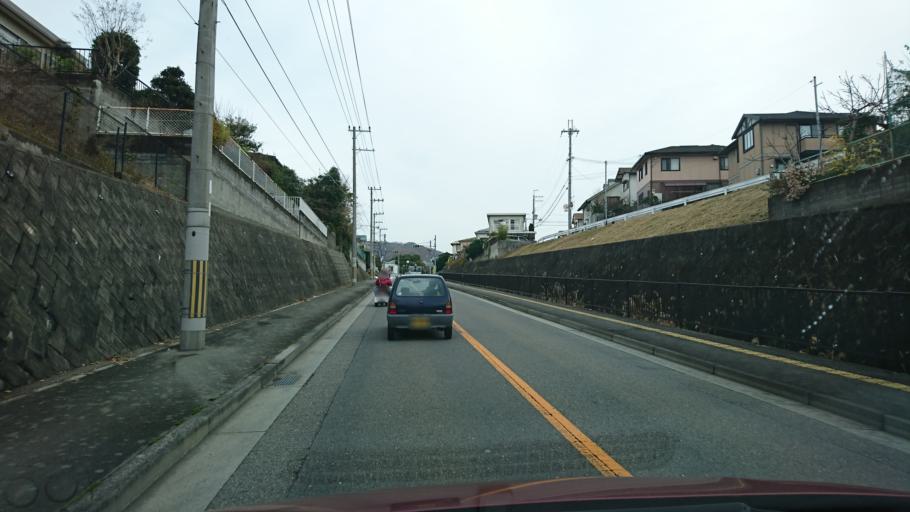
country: JP
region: Osaka
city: Ikeda
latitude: 34.8984
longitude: 135.4381
